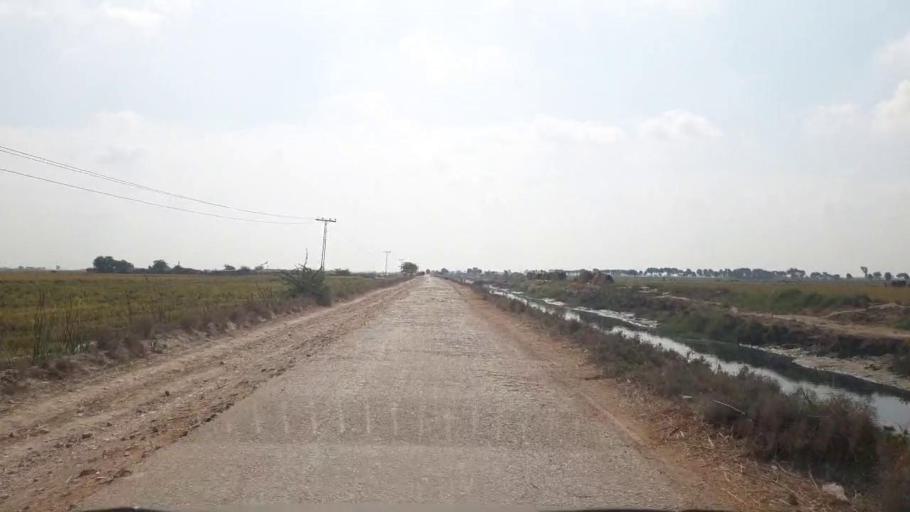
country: PK
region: Sindh
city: Kario
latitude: 24.6306
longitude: 68.5510
